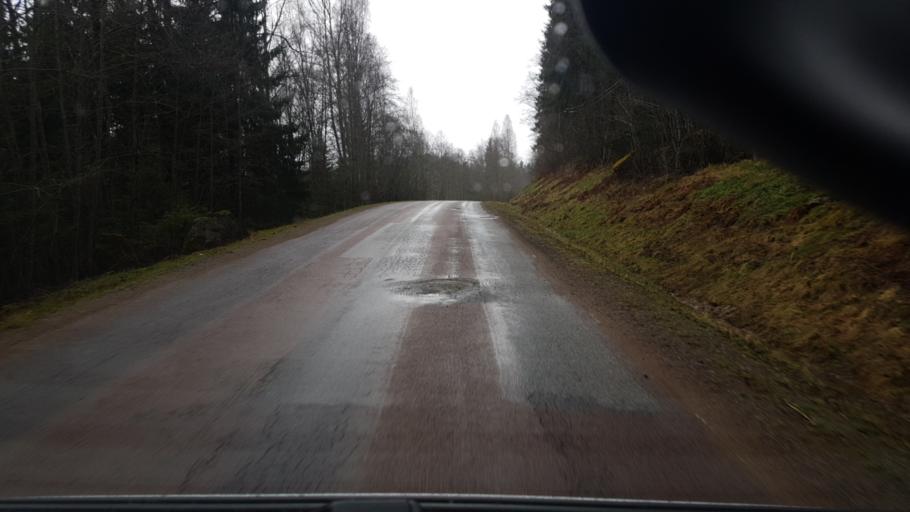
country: SE
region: Vaermland
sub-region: Eda Kommun
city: Amotfors
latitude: 59.9018
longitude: 12.5247
